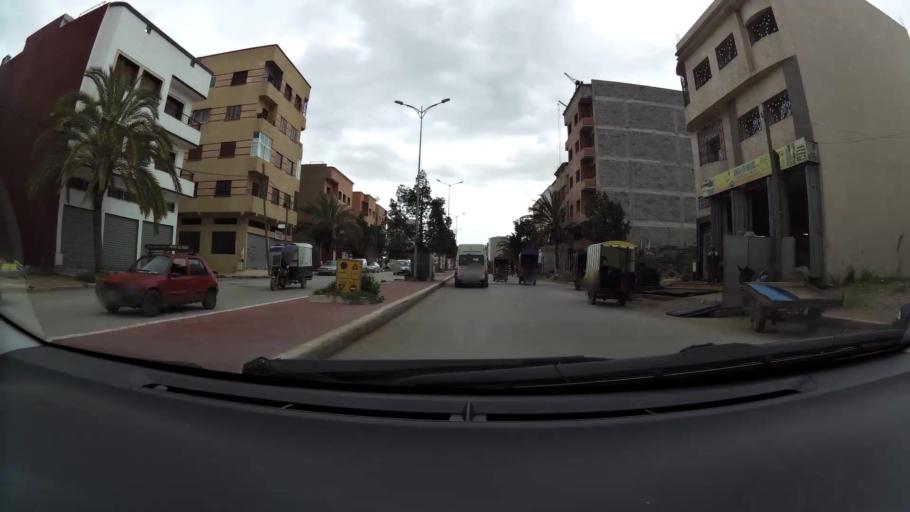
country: MA
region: Grand Casablanca
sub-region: Mediouna
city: Tit Mellil
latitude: 33.5551
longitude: -7.5350
